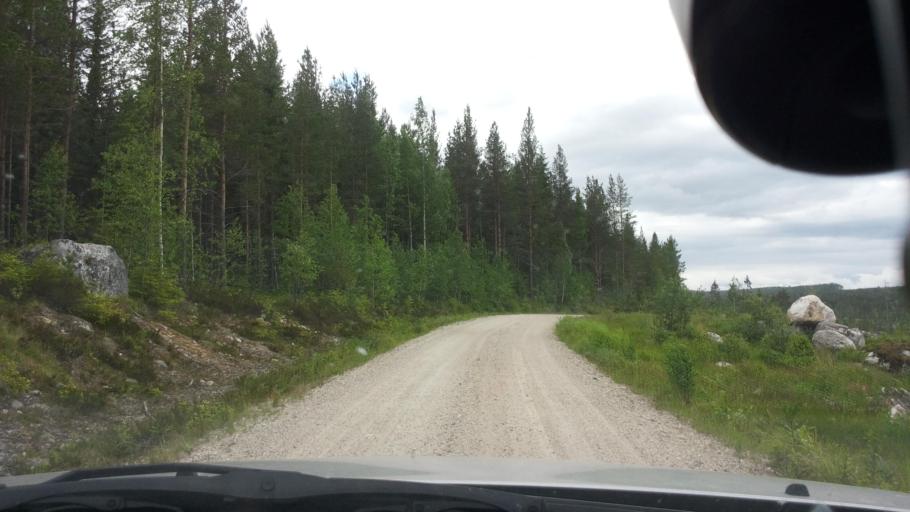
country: SE
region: Gaevleborg
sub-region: Ovanakers Kommun
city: Edsbyn
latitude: 61.4806
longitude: 15.3123
